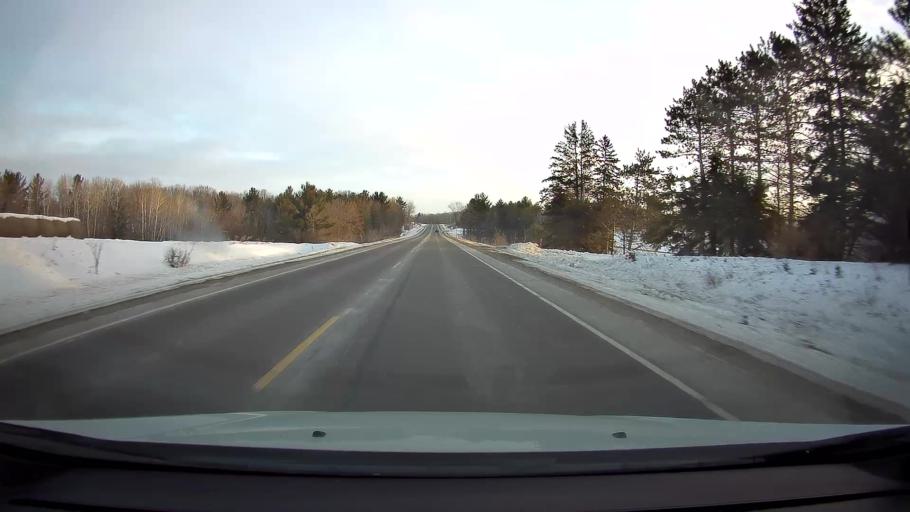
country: US
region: Wisconsin
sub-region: Polk County
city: Clear Lake
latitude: 45.2615
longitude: -92.2578
